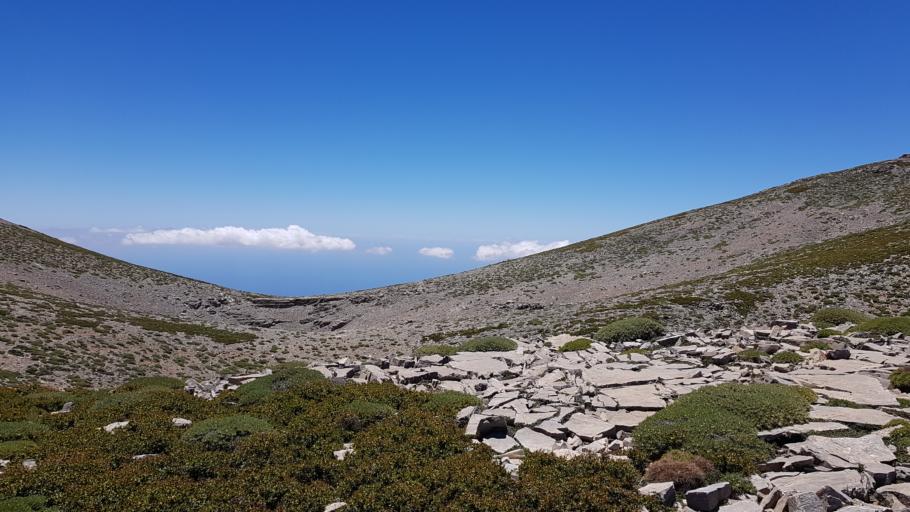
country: GR
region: Crete
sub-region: Nomos Rethymnis
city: Zoniana
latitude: 35.2237
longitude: 24.7806
